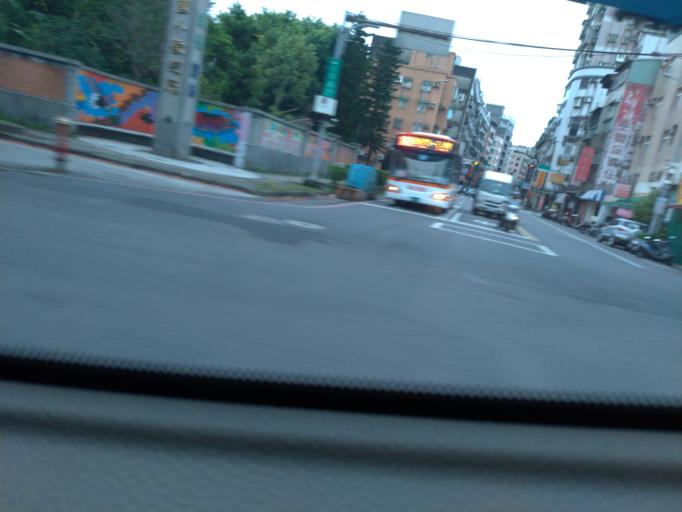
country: TW
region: Taiwan
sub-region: Taoyuan
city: Taoyuan
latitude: 24.9304
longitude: 121.3786
